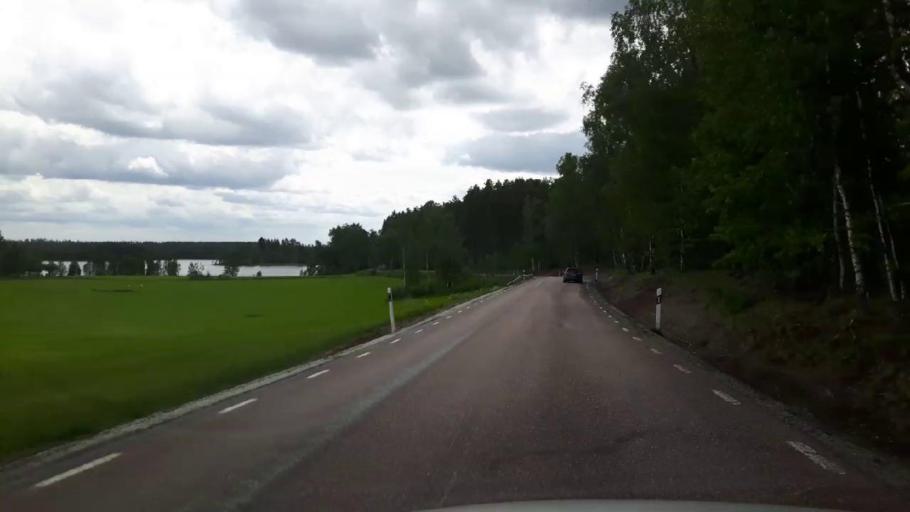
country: SE
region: Vaestmanland
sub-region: Skinnskattebergs Kommun
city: Skinnskatteberg
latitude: 59.8571
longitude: 15.8418
